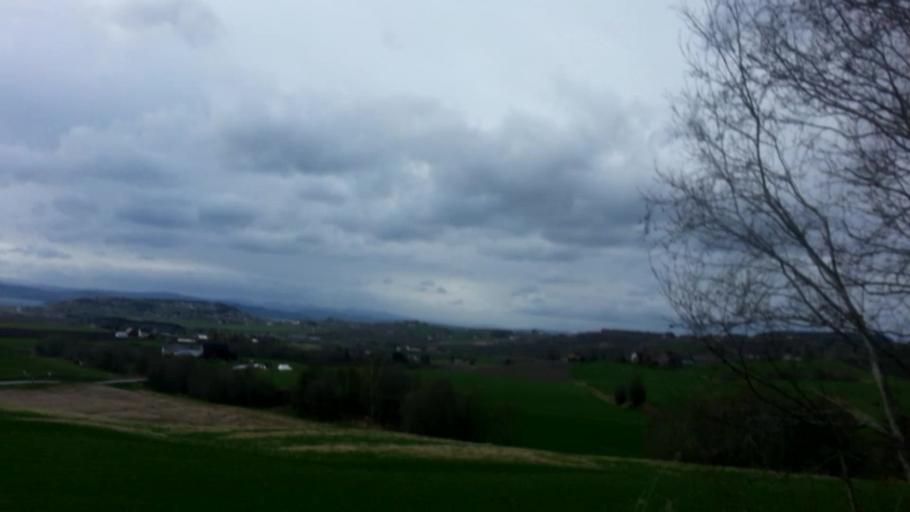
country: NO
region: Nord-Trondelag
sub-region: Levanger
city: Skogn
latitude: 63.6615
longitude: 11.2267
